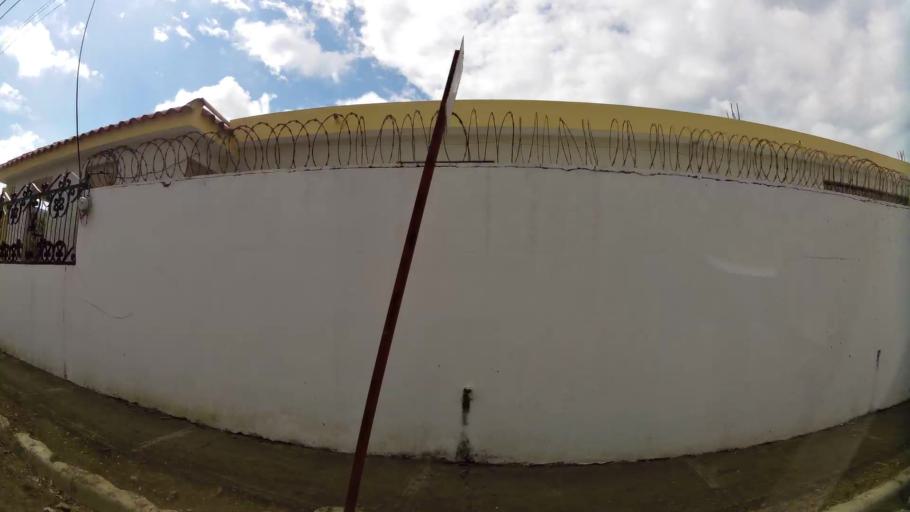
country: DO
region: Santiago
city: Palmar Arriba
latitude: 19.4906
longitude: -70.7298
